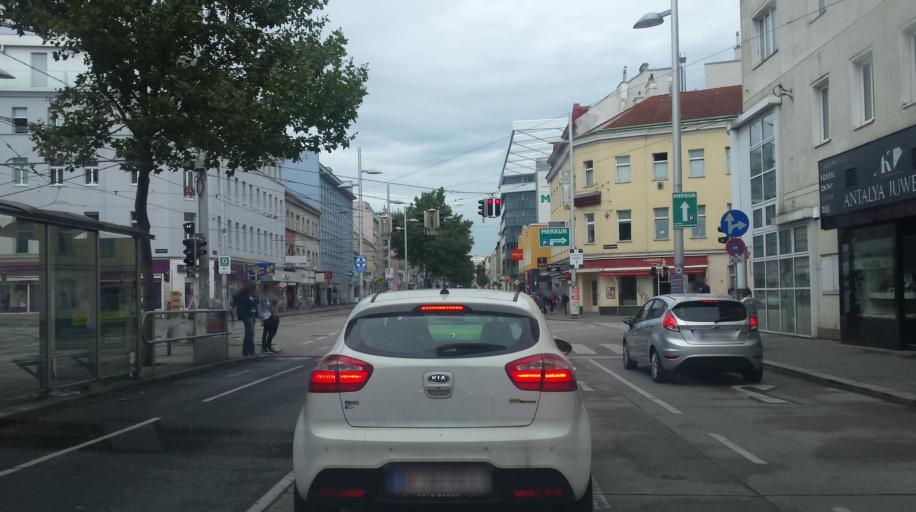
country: AT
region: Vienna
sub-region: Wien Stadt
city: Vienna
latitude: 48.1738
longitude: 16.4167
